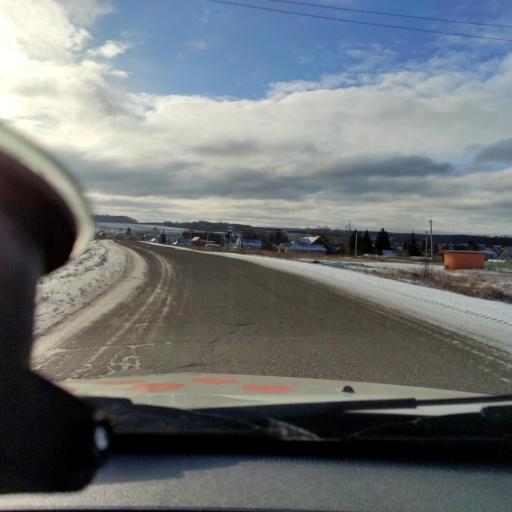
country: RU
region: Bashkortostan
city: Mikhaylovka
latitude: 54.8048
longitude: 55.7794
